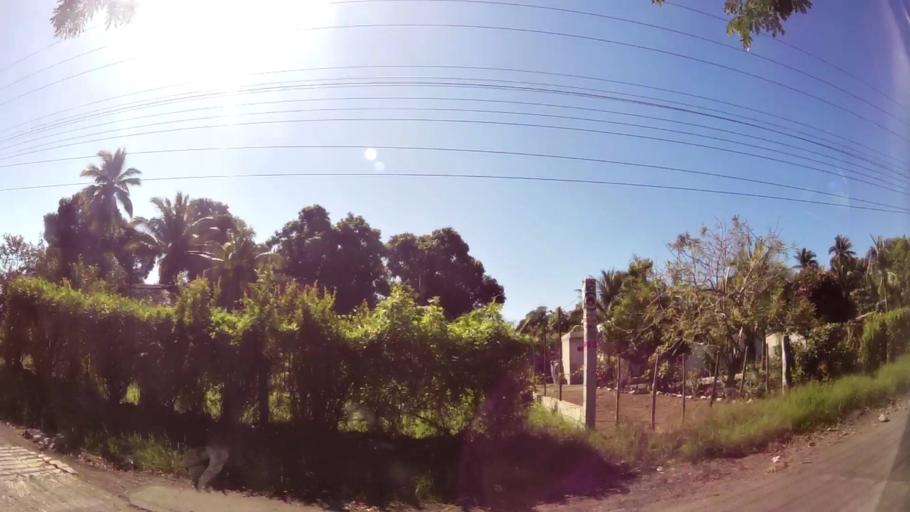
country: GT
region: Escuintla
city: Iztapa
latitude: 13.9241
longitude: -90.5812
